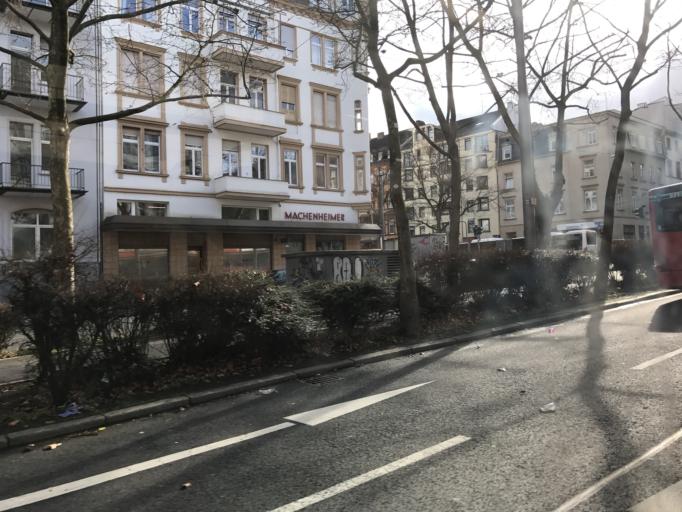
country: DE
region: Hesse
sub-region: Regierungsbezirk Darmstadt
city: Wiesbaden
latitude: 50.0788
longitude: 8.2296
